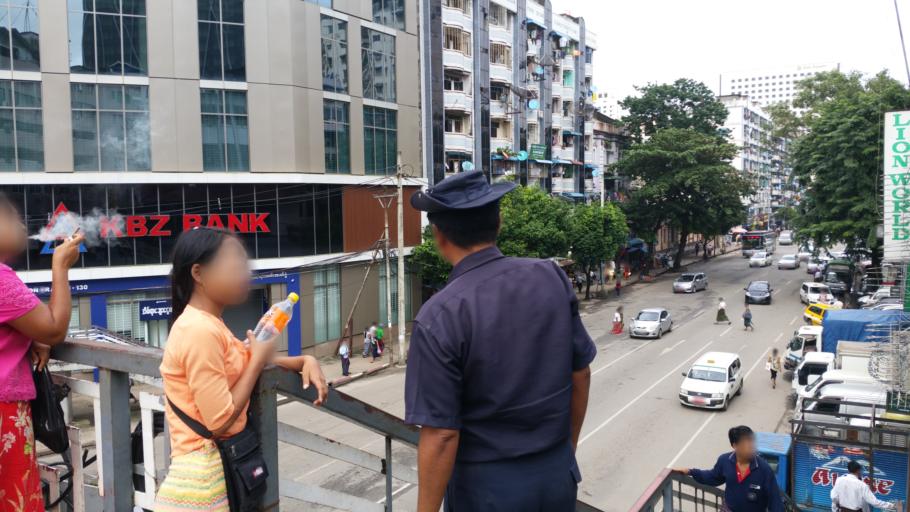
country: MM
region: Yangon
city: Yangon
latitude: 16.7770
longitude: 96.1533
